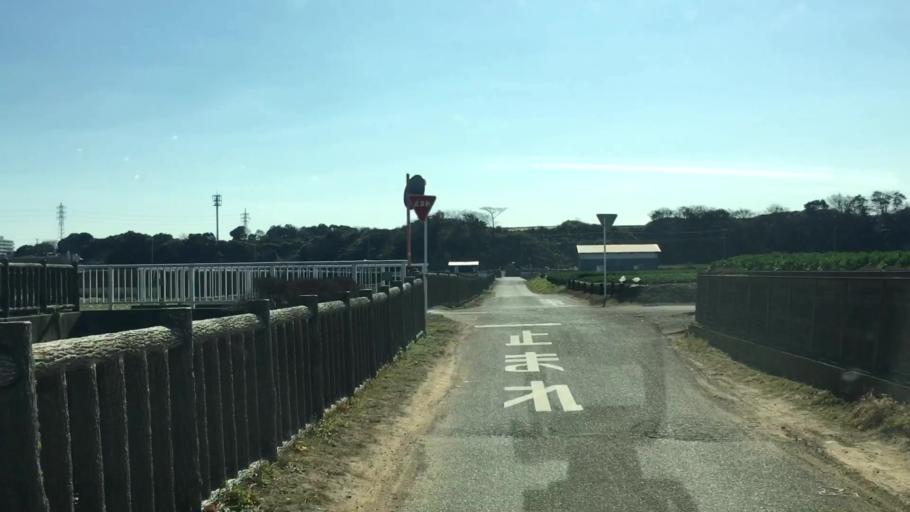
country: JP
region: Kanagawa
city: Miura
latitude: 35.2017
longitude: 139.6222
